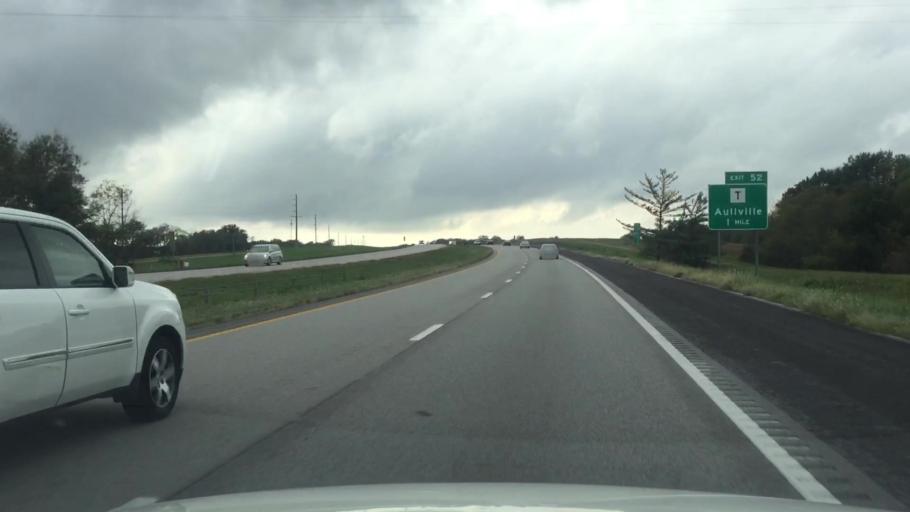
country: US
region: Missouri
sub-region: Lafayette County
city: Concordia
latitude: 38.9916
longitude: -93.6495
